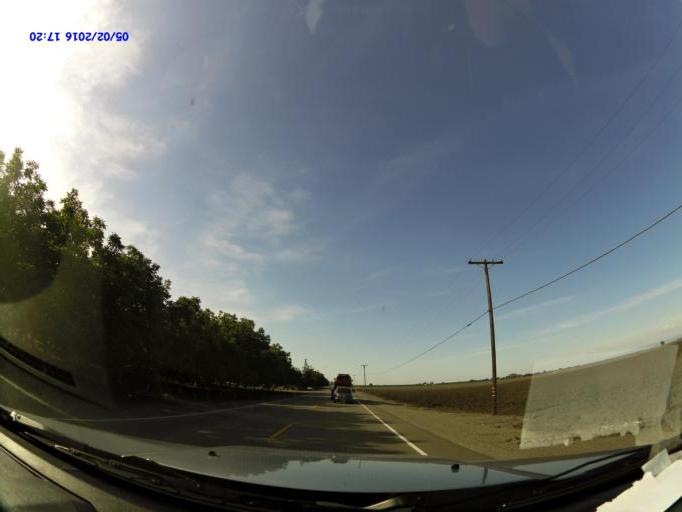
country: US
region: California
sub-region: San Joaquin County
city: Manteca
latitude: 37.8386
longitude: -121.1448
